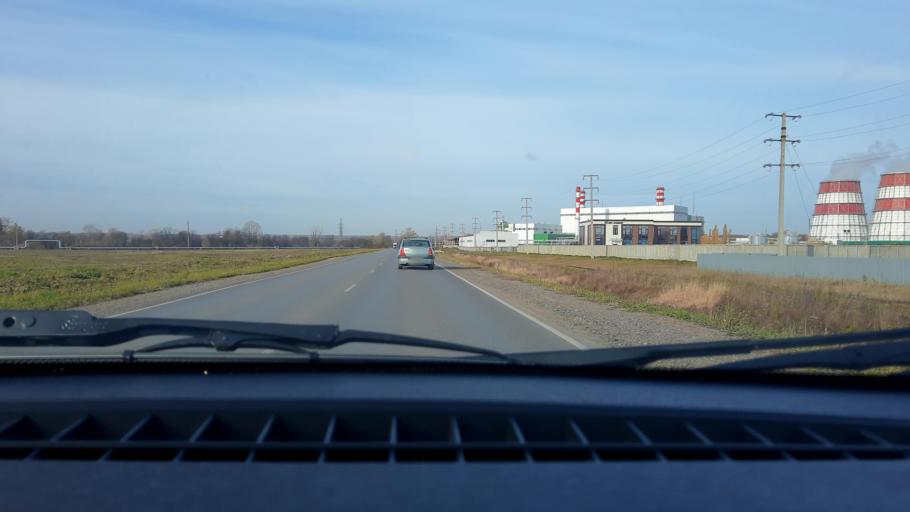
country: RU
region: Bashkortostan
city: Mikhaylovka
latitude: 54.7994
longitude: 55.8486
